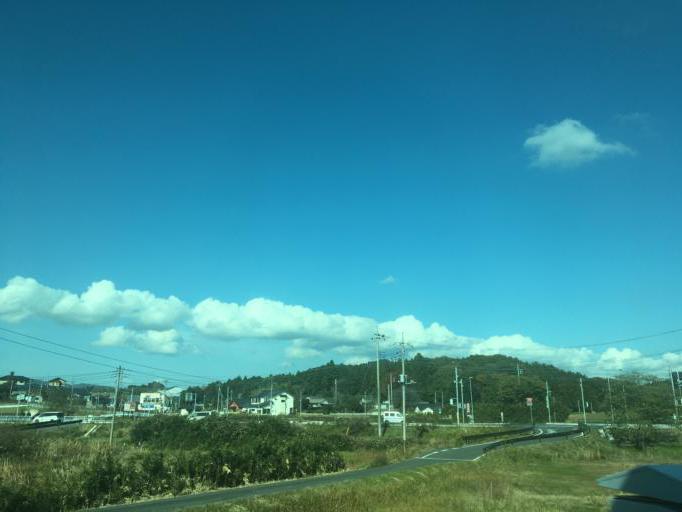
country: JP
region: Ibaraki
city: Kasama
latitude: 36.3647
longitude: 140.2621
